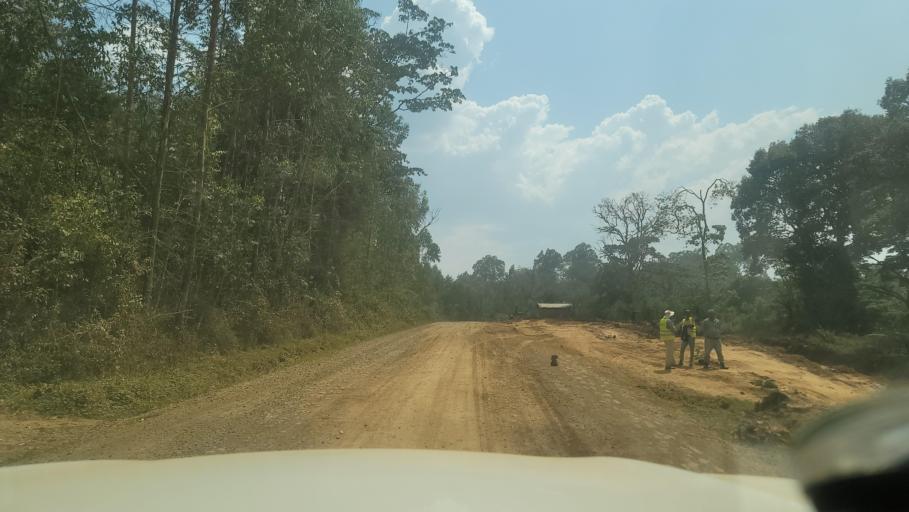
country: ET
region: Oromiya
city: Agaro
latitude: 7.7604
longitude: 36.2871
